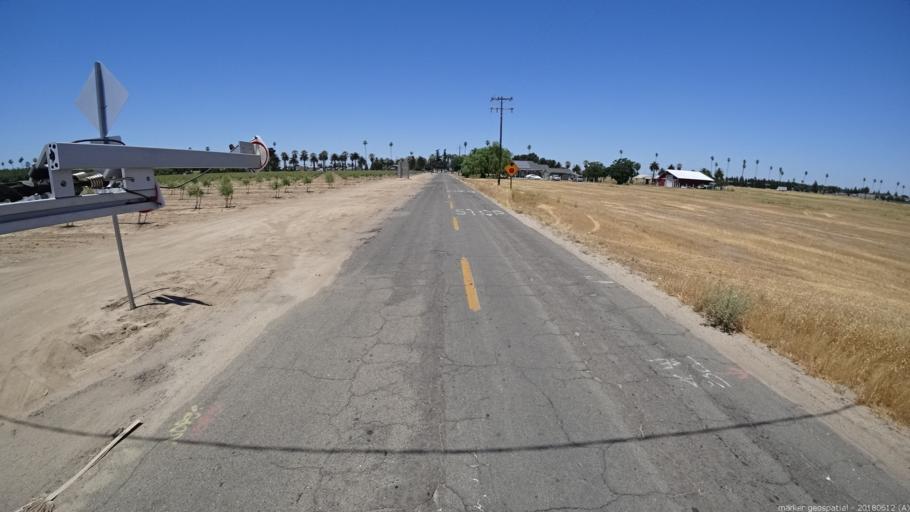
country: US
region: California
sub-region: Madera County
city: Chowchilla
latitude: 37.1038
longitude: -120.2763
